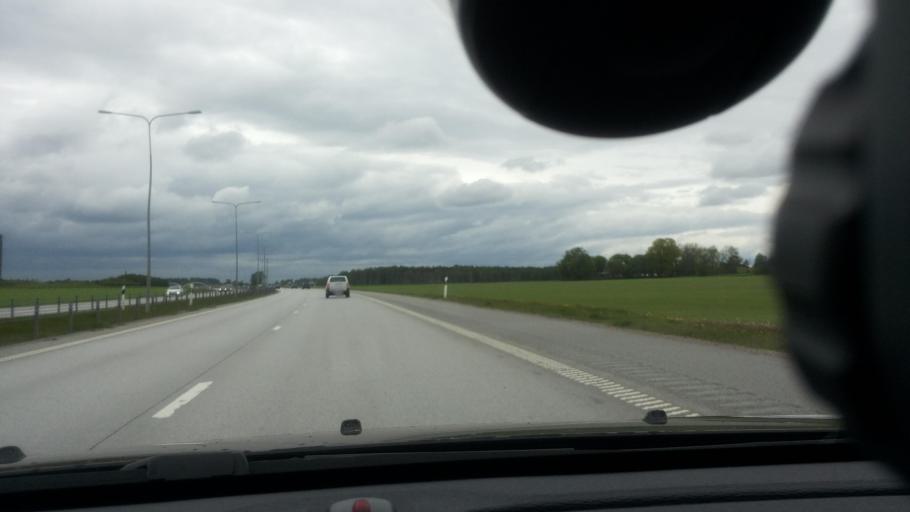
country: SE
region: Uppsala
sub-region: Uppsala Kommun
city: Saevja
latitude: 59.8596
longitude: 17.7269
